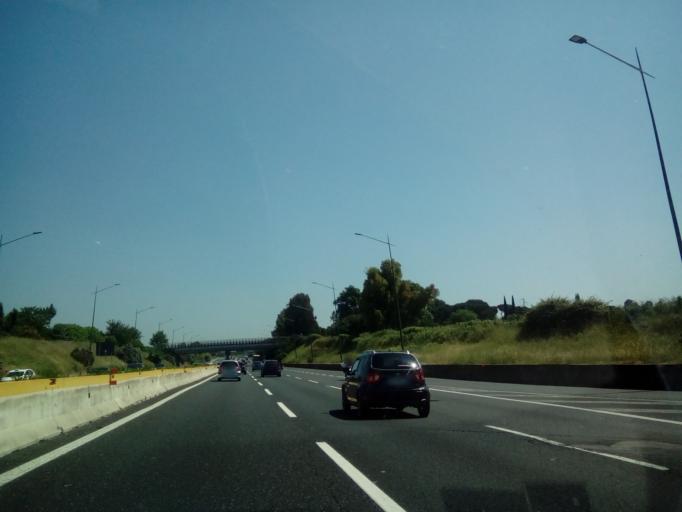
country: IT
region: Latium
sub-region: Citta metropolitana di Roma Capitale
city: Valle Santa
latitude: 41.9601
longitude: 12.3899
